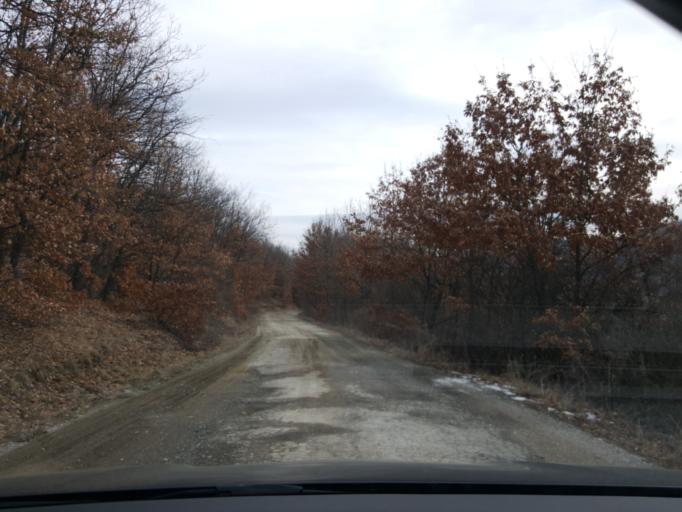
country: RS
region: Central Serbia
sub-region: Pirotski Okrug
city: Dimitrovgrad
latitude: 42.9985
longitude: 22.7468
